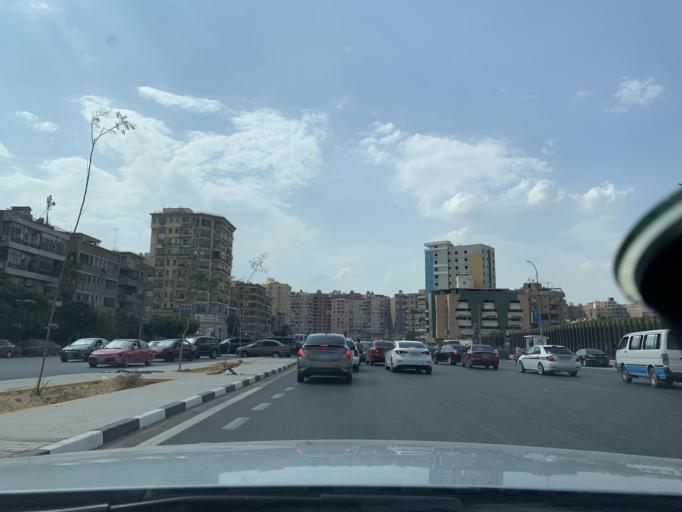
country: EG
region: Muhafazat al Qalyubiyah
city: Al Khankah
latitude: 30.1161
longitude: 31.3425
